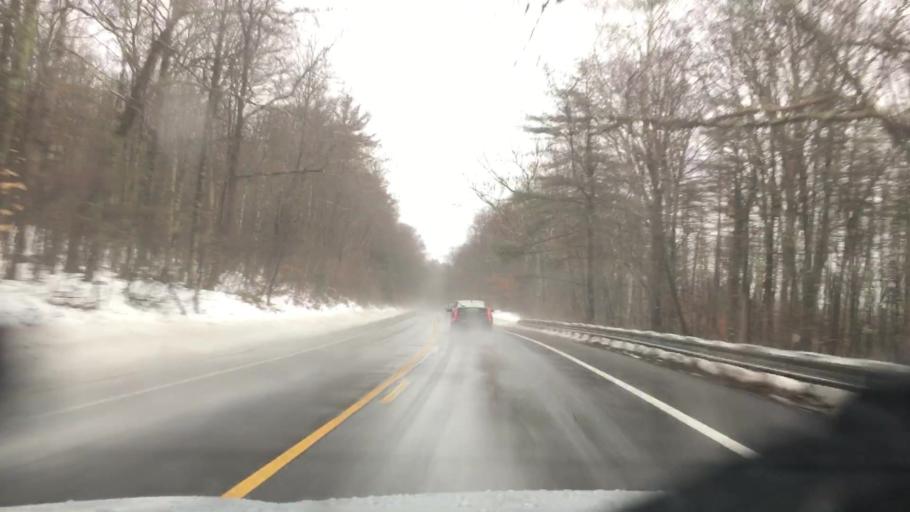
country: US
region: Massachusetts
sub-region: Franklin County
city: Shutesbury
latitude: 42.4434
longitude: -72.3876
